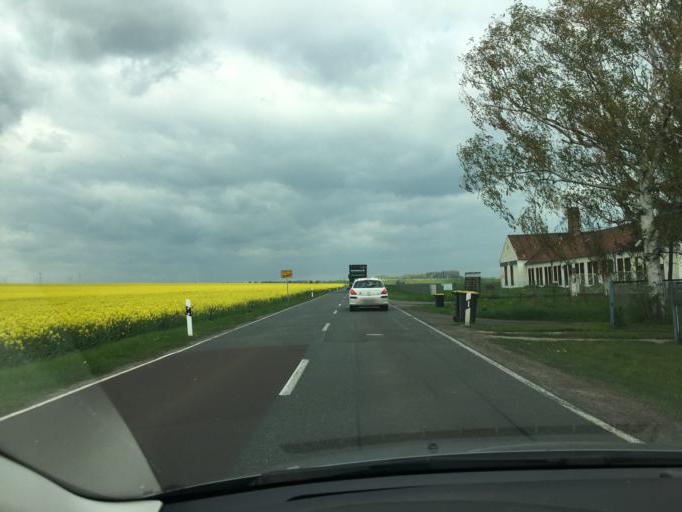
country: DE
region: Saxony-Anhalt
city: Giersleben
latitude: 51.7805
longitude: 11.5792
